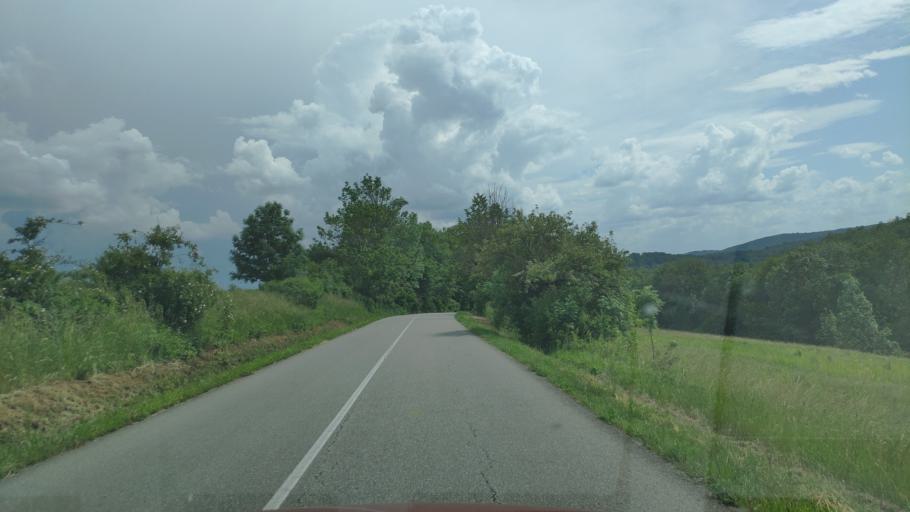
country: SK
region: Kosicky
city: Medzev
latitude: 48.6951
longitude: 20.9736
